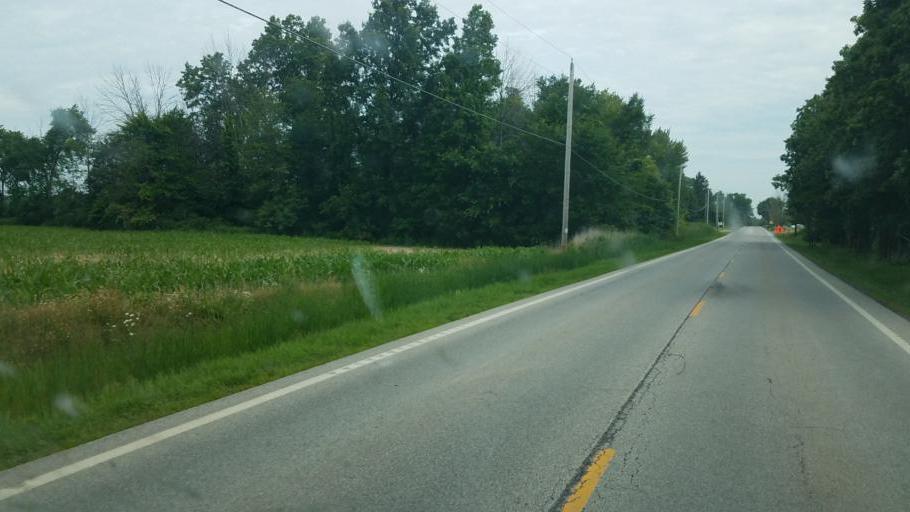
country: US
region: Ohio
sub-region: Lorain County
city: Grafton
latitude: 41.1947
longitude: -82.0229
